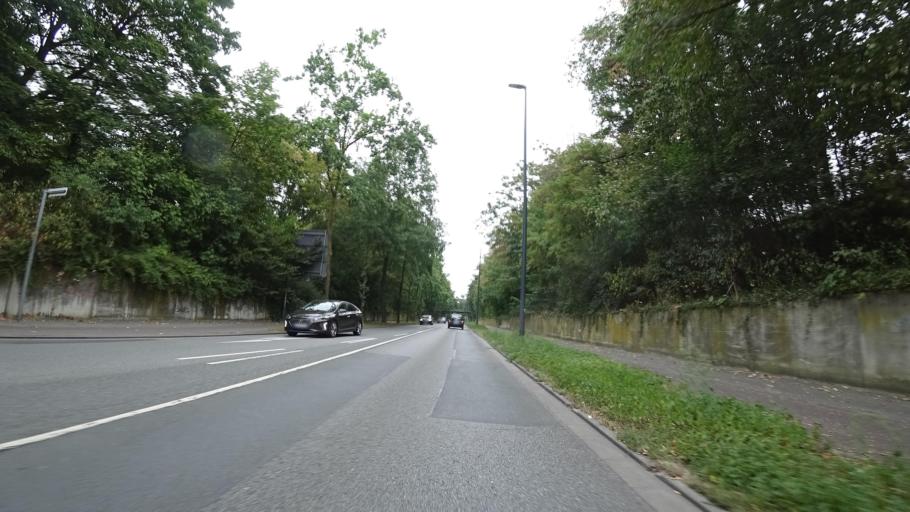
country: DE
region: North Rhine-Westphalia
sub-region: Regierungsbezirk Detmold
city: Guetersloh
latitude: 51.9067
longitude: 8.4063
